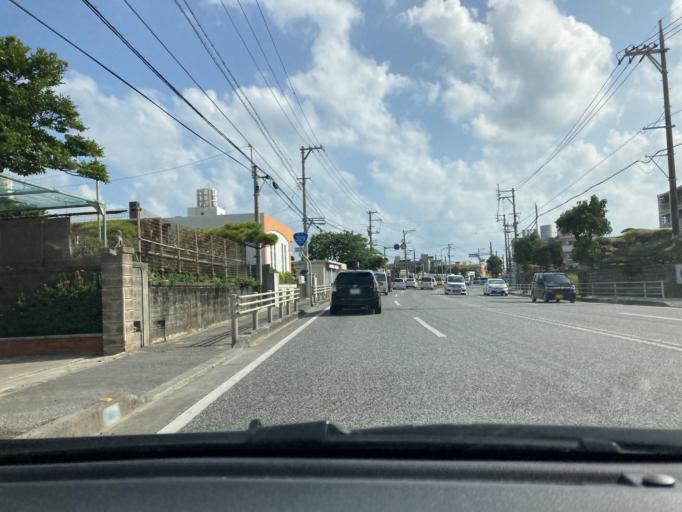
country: JP
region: Okinawa
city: Chatan
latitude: 26.2845
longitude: 127.8155
